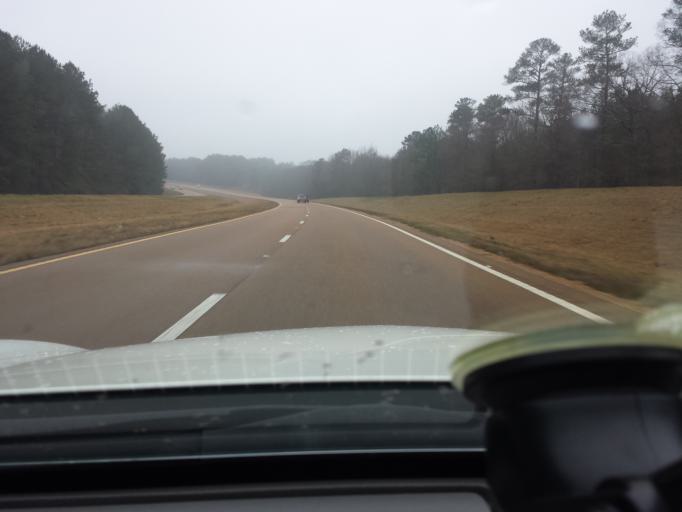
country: US
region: Mississippi
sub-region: Leake County
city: Carthage
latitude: 32.6306
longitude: -89.6842
